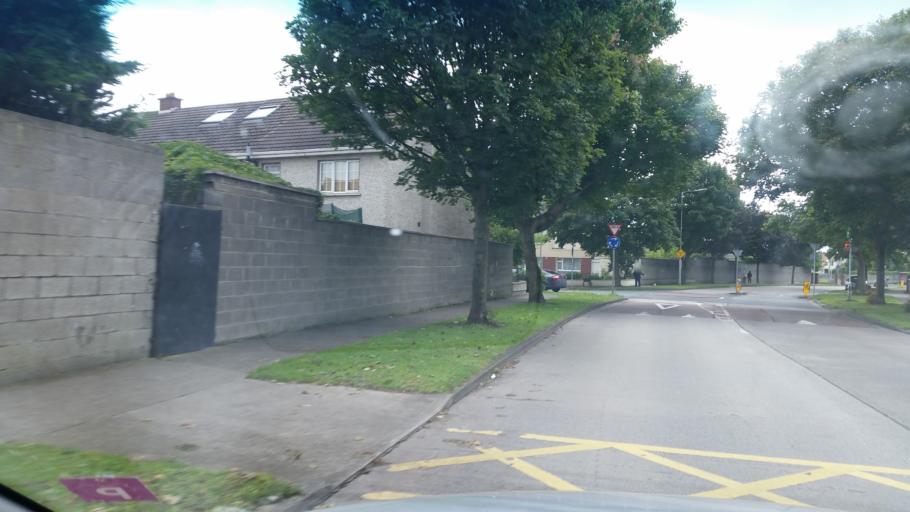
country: IE
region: Leinster
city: Raheny
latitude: 53.3952
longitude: -6.1789
